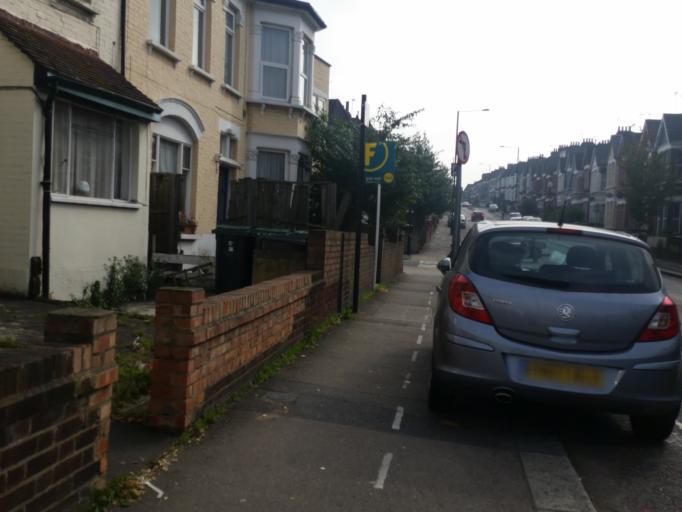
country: GB
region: England
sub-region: Greater London
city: Harringay
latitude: 51.5813
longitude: -0.1059
